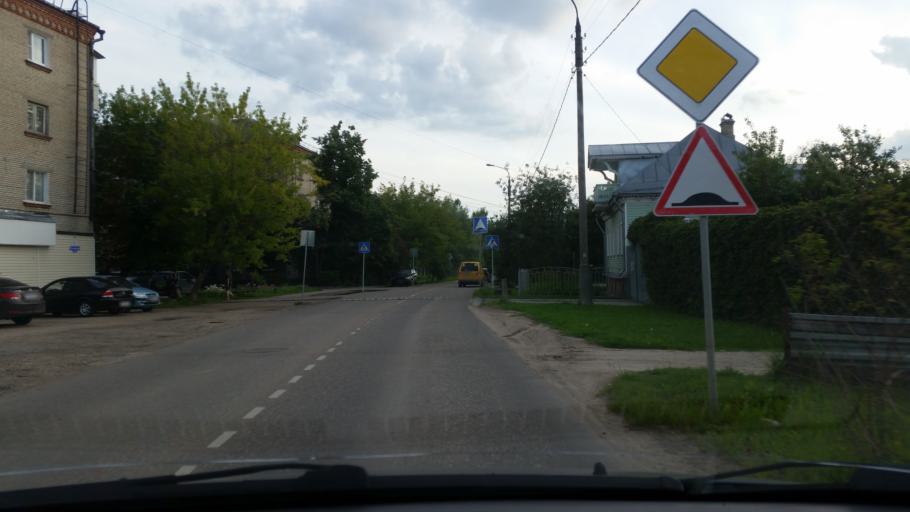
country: RU
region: Moskovskaya
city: Serpukhov
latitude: 54.9290
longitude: 37.4370
